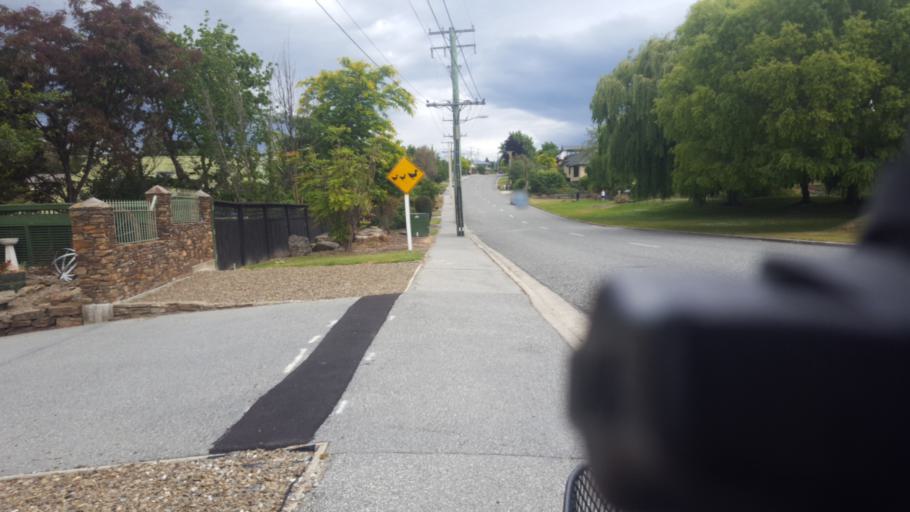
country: NZ
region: Otago
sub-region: Queenstown-Lakes District
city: Wanaka
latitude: -45.2600
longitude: 169.3804
